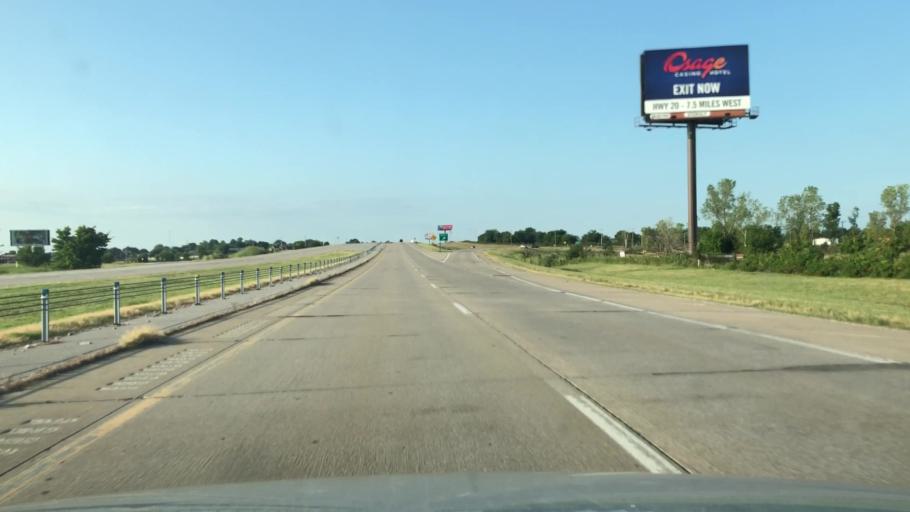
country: US
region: Oklahoma
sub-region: Osage County
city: Skiatook
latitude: 36.3697
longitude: -95.9208
